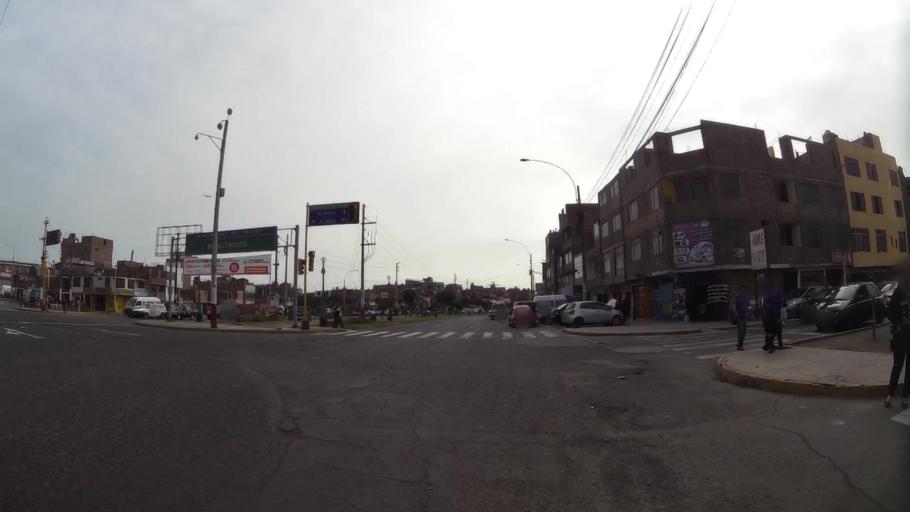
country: PE
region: Callao
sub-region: Callao
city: Callao
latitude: -12.0298
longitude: -77.0944
